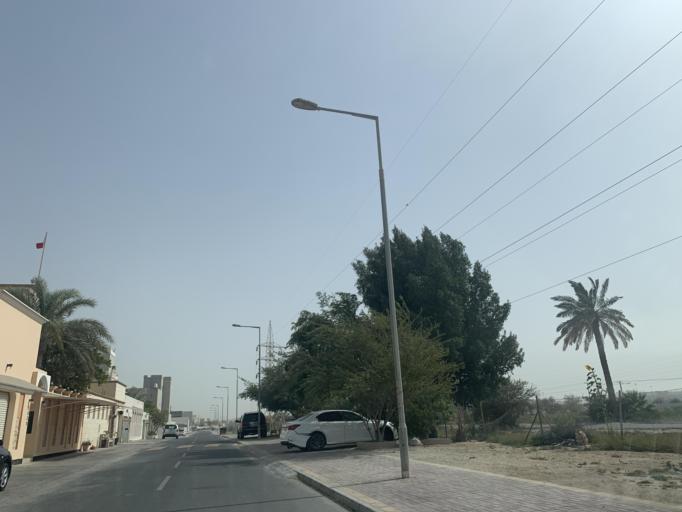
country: BH
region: Northern
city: Madinat `Isa
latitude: 26.1665
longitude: 50.5362
